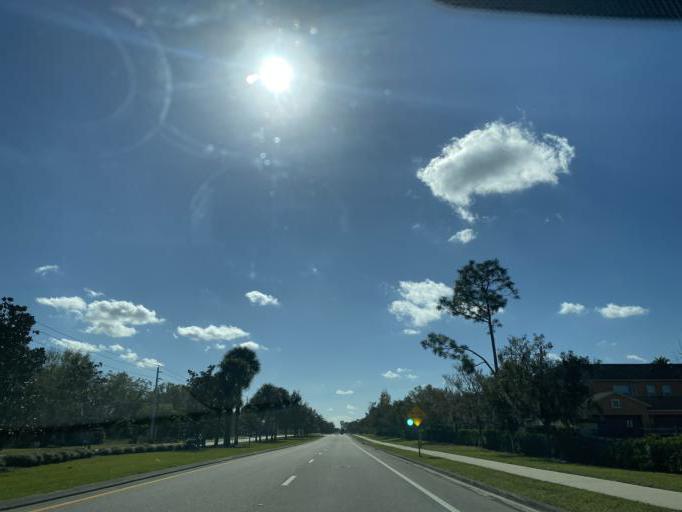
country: US
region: Florida
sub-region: Seminole County
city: Heathrow
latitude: 28.8072
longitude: -81.3481
